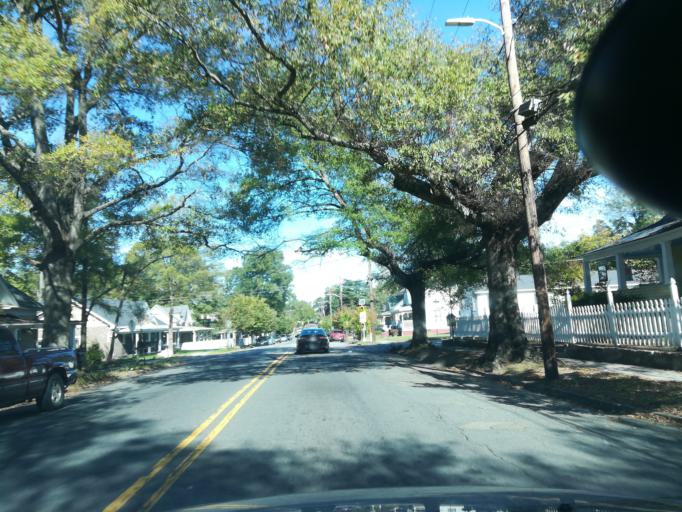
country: US
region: North Carolina
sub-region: Durham County
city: Durham
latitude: 35.9839
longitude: -78.8777
